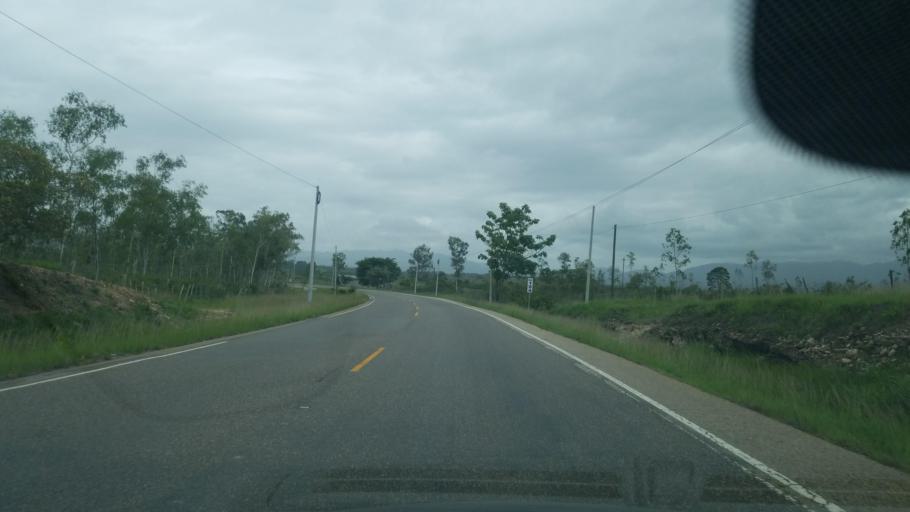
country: HN
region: Ocotepeque
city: Lucerna
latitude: 14.5289
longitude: -88.9514
